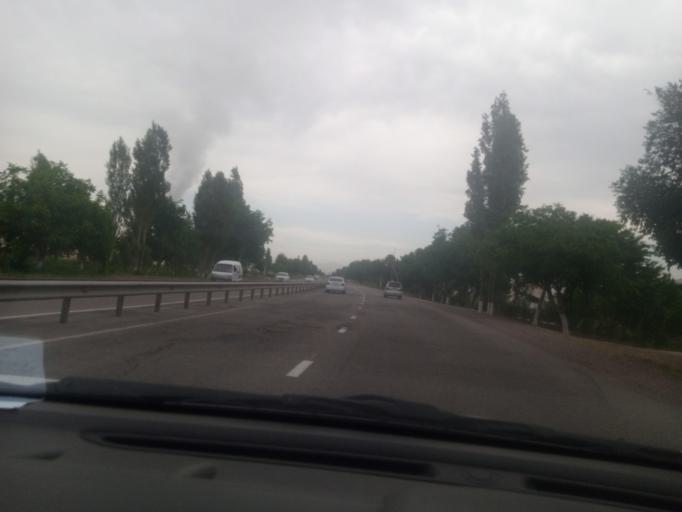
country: UZ
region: Toshkent
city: Ohangaron
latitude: 40.9080
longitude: 69.7699
